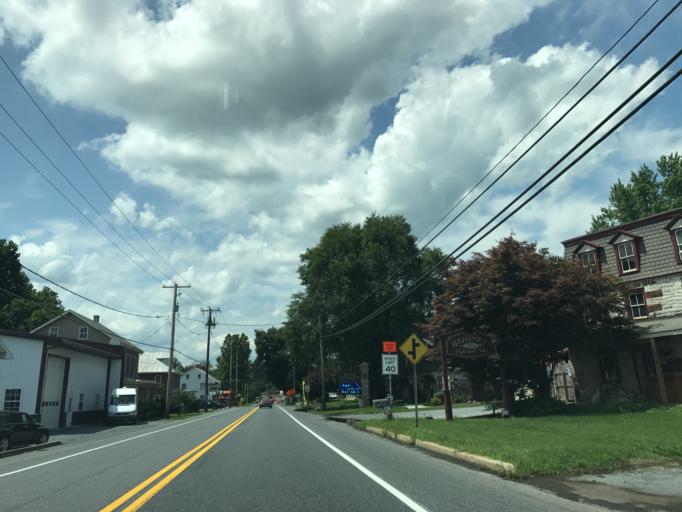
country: US
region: Pennsylvania
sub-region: Lancaster County
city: Clay
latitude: 40.2178
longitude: -76.2532
